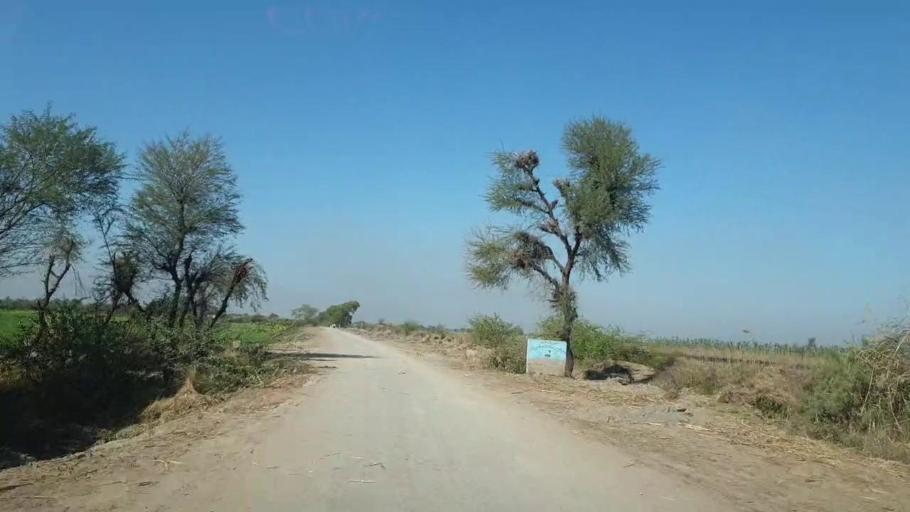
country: PK
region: Sindh
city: Mirpur Khas
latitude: 25.6049
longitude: 69.0273
